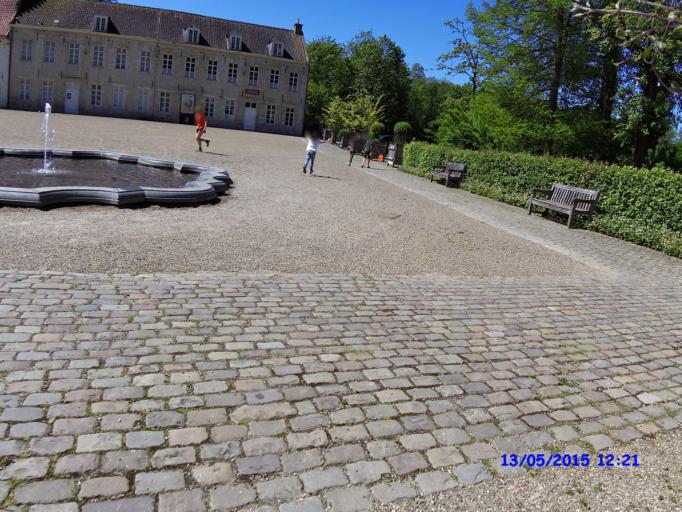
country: BE
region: Flanders
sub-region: Provincie Vlaams-Brabant
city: Hoeilaart
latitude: 50.8139
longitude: 4.4438
